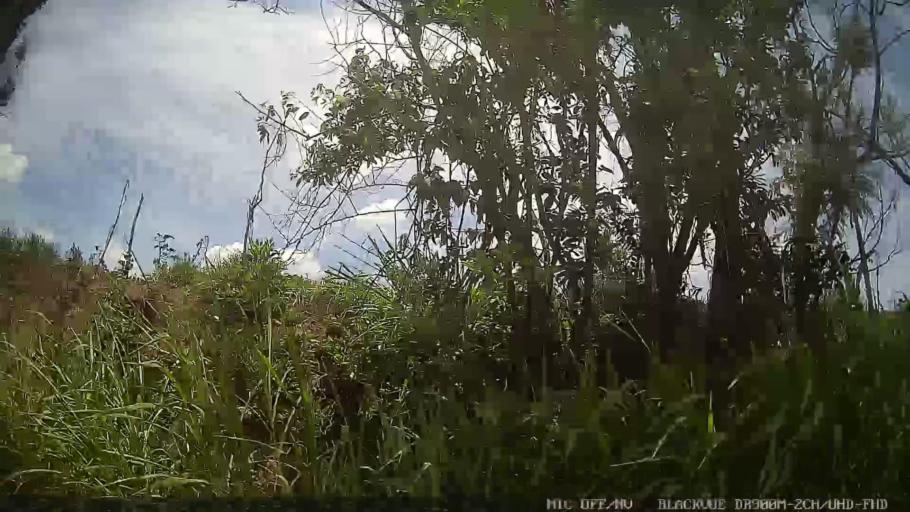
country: BR
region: Sao Paulo
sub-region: Atibaia
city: Atibaia
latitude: -23.0920
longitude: -46.6173
